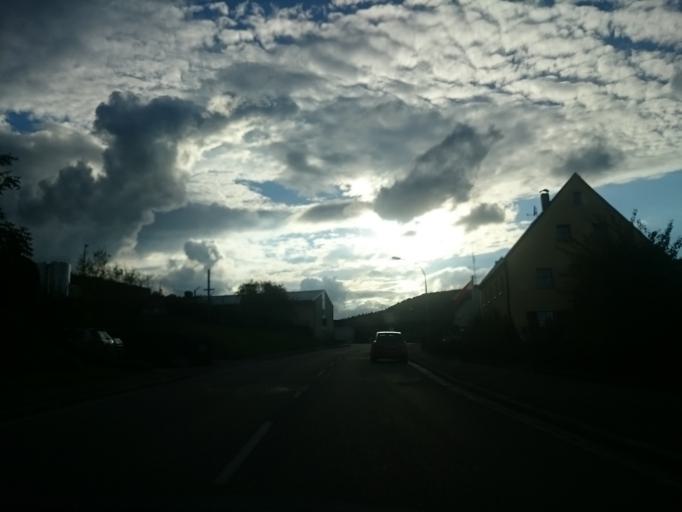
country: DE
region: Bavaria
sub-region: Regierungsbezirk Mittelfranken
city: Thalmassing
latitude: 49.0834
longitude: 11.2124
